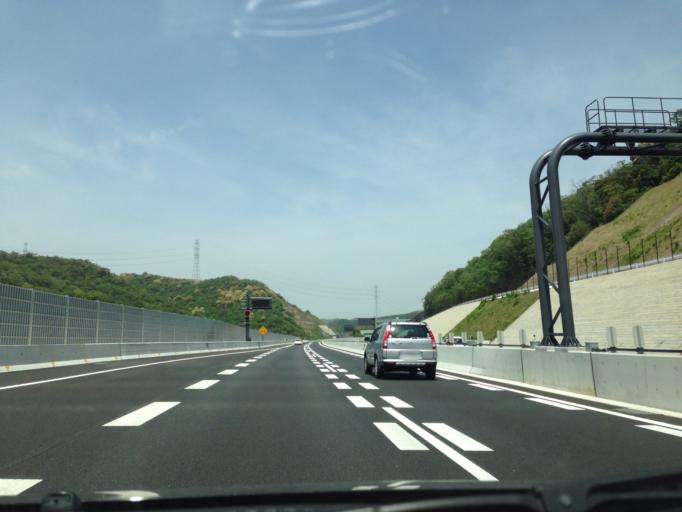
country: JP
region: Aichi
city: Gamagori
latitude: 34.9225
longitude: 137.2729
